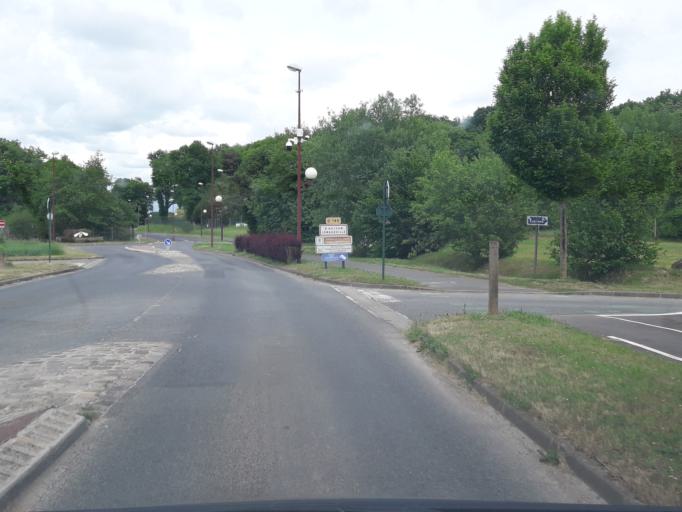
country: FR
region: Ile-de-France
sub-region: Departement de l'Essonne
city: Cerny
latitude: 48.4535
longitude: 2.3152
